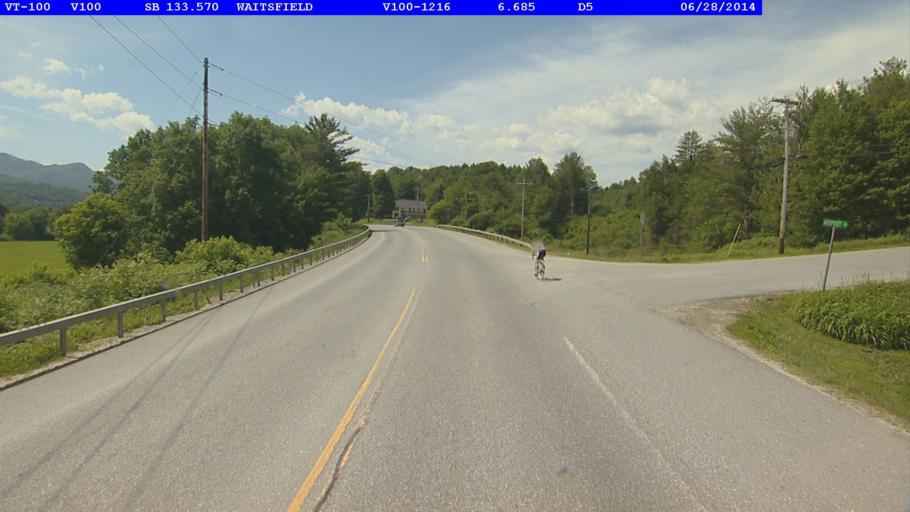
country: US
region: Vermont
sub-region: Washington County
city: Waterbury
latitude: 44.2239
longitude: -72.7890
